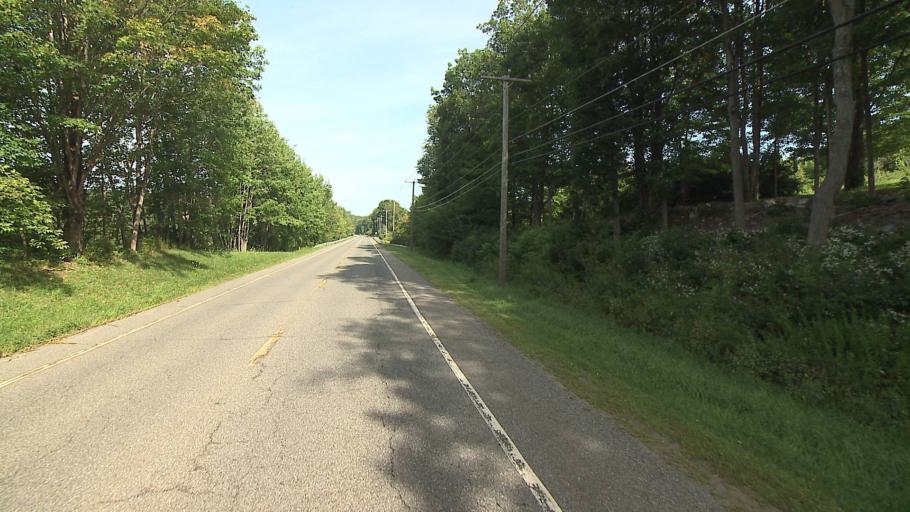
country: US
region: Connecticut
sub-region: Litchfield County
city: Litchfield
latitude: 41.7331
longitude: -73.1585
